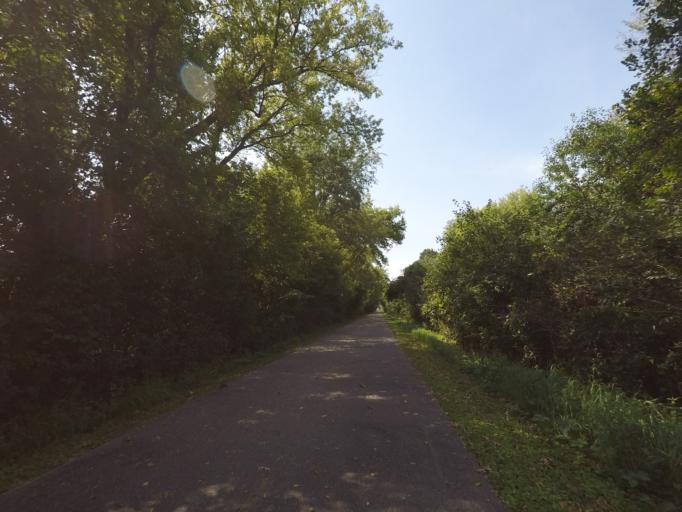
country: US
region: Wisconsin
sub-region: Jefferson County
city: Fort Atkinson
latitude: 42.8976
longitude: -88.8635
